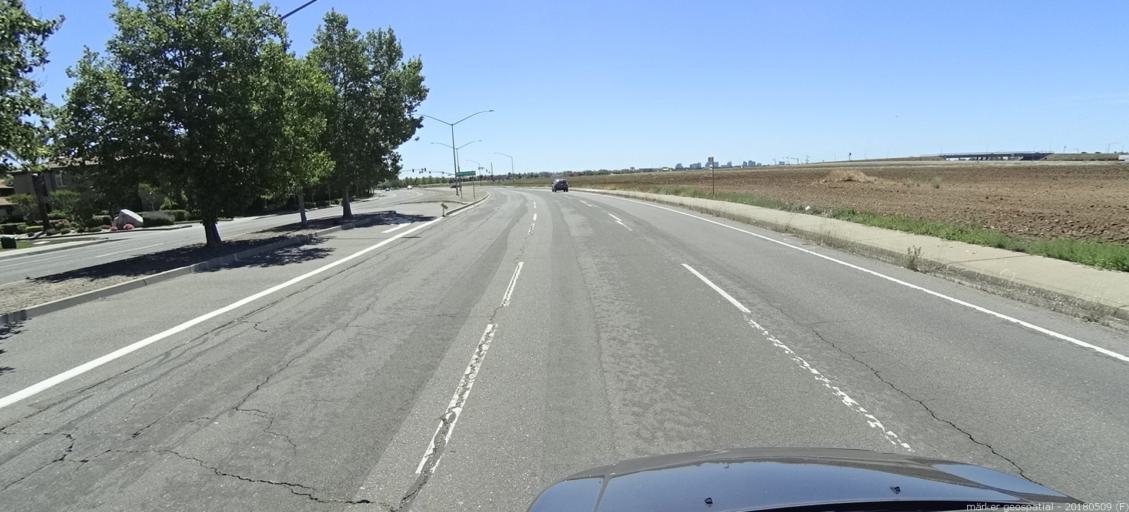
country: US
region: California
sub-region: Yolo County
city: West Sacramento
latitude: 38.6490
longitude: -121.5254
